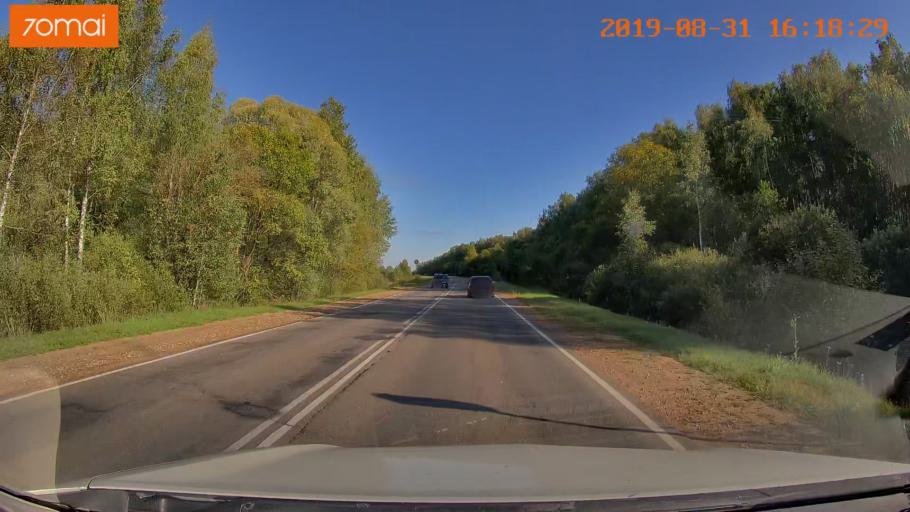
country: RU
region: Kaluga
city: Nikola-Lenivets
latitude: 54.5361
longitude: 35.5557
